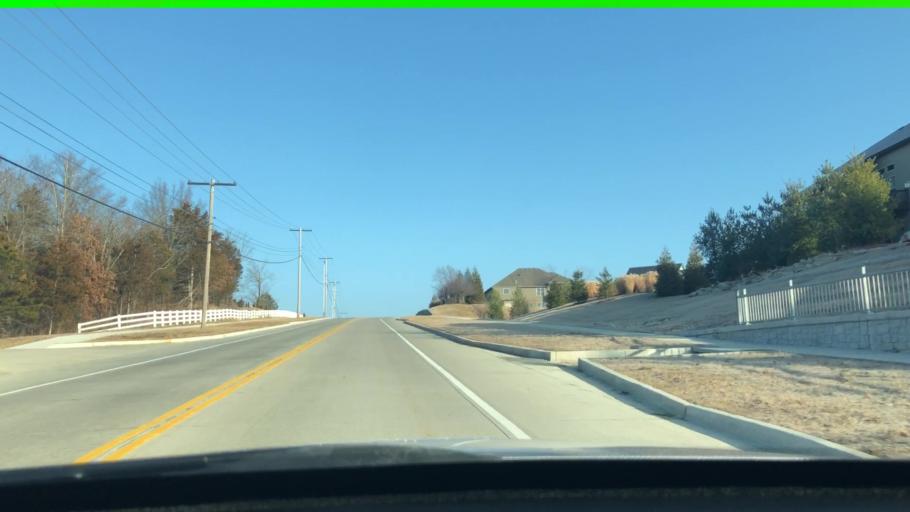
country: US
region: Missouri
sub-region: Boone County
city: Columbia
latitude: 38.9076
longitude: -92.4004
